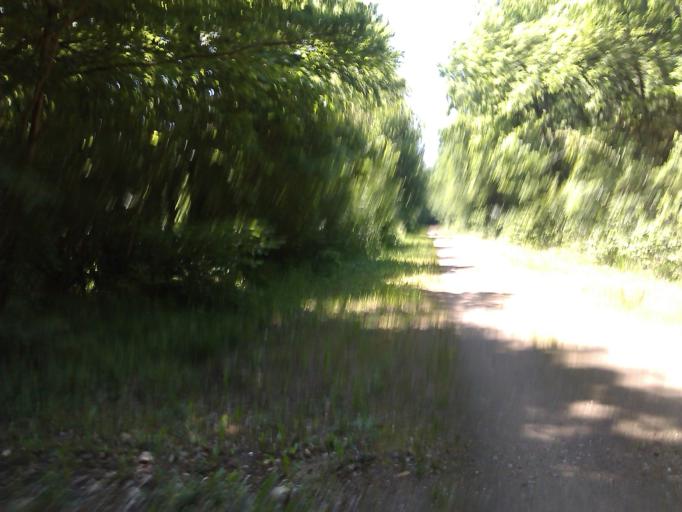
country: FR
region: Centre
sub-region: Departement de l'Indre
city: Saint-Gaultier
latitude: 46.6389
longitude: 1.3798
